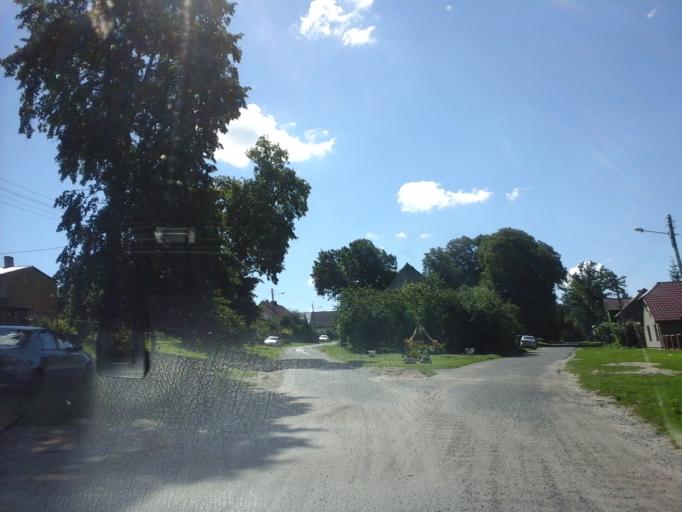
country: PL
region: West Pomeranian Voivodeship
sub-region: Powiat choszczenski
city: Recz
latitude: 53.2188
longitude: 15.4923
